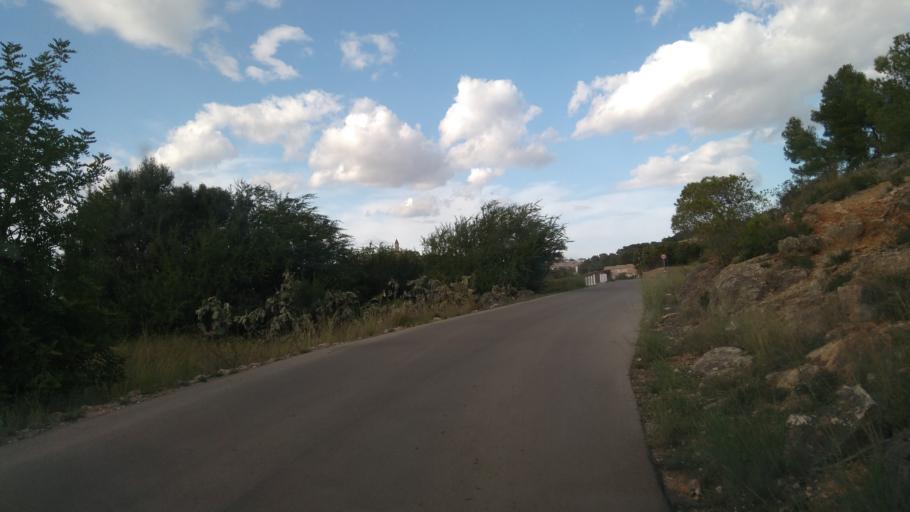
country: ES
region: Valencia
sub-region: Provincia de Valencia
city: Alzira
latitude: 39.1434
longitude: -0.4149
